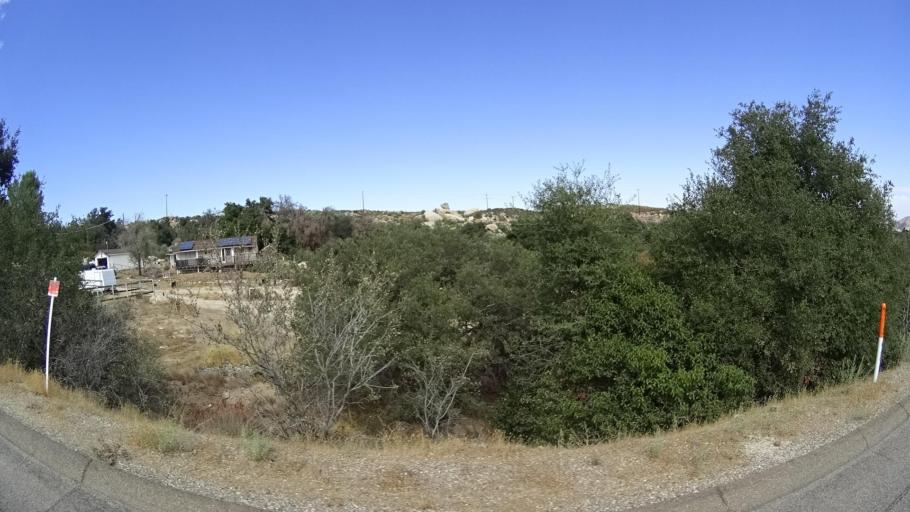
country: MX
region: Baja California
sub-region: Tecate
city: Cereso del Hongo
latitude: 32.6671
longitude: -116.2851
